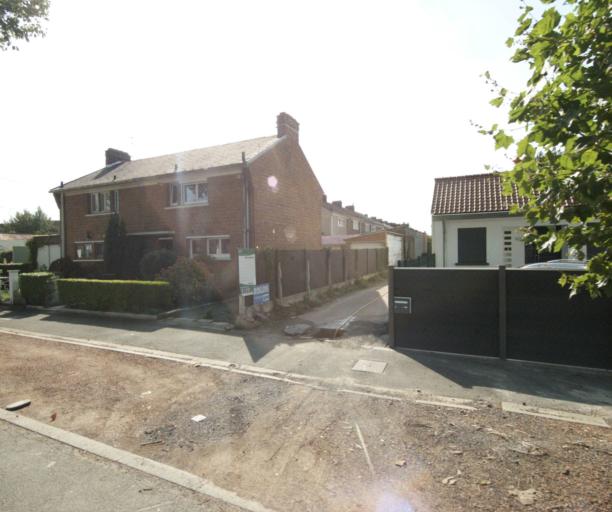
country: FR
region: Nord-Pas-de-Calais
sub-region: Departement du Nord
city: Capinghem
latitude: 50.6459
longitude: 2.9618
